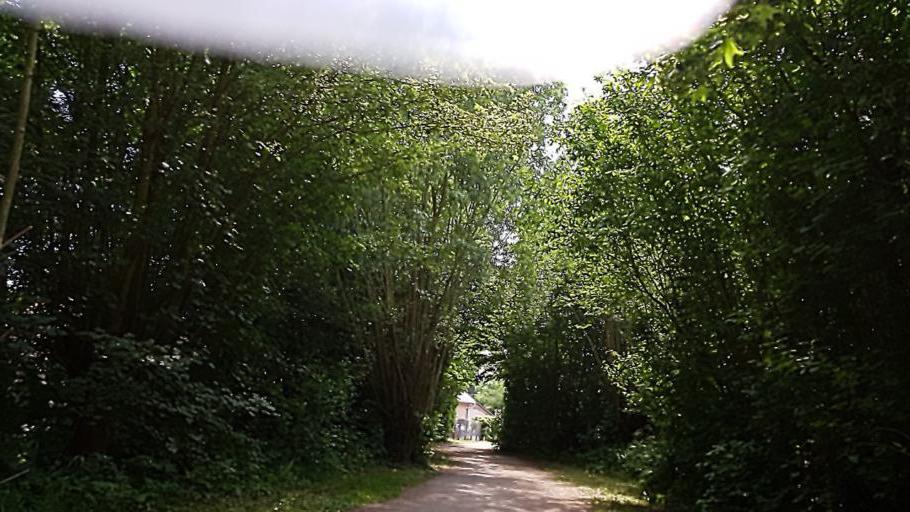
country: FR
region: Nord-Pas-de-Calais
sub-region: Departement du Nord
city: Vieux-Conde
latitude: 50.4739
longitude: 3.5717
